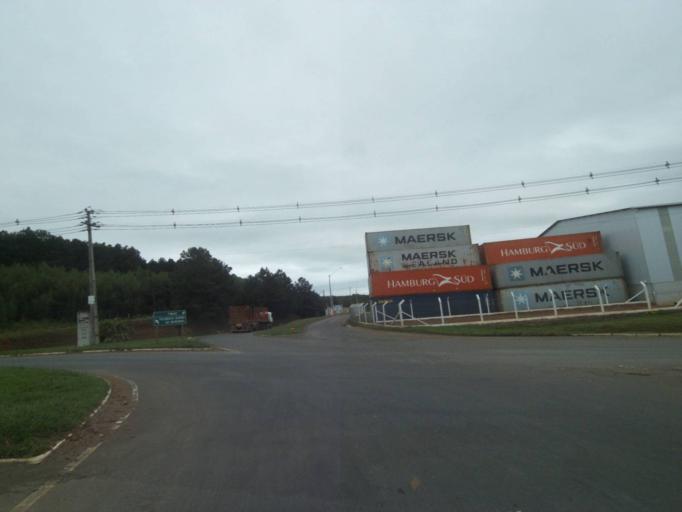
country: BR
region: Parana
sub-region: Telemaco Borba
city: Telemaco Borba
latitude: -24.3804
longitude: -50.6704
